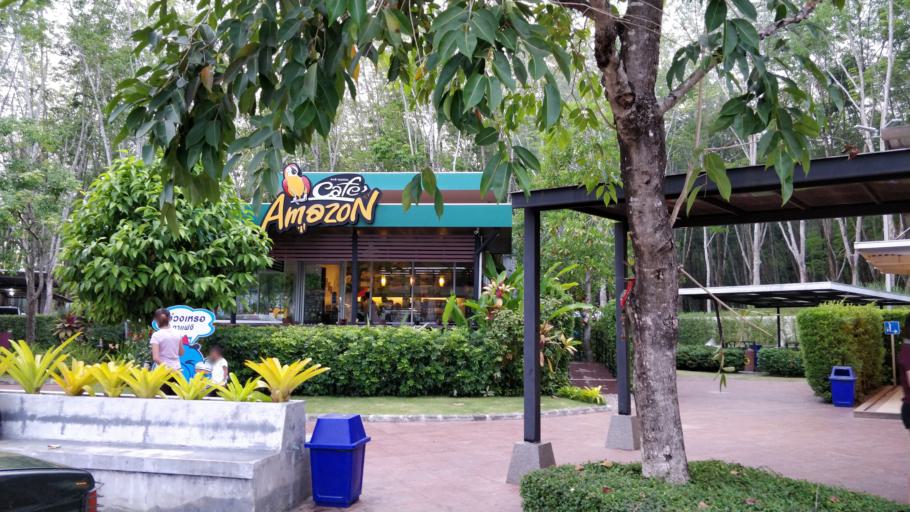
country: TH
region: Prachuap Khiri Khan
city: Bang Saphan Noi
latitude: 10.9306
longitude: 99.2893
